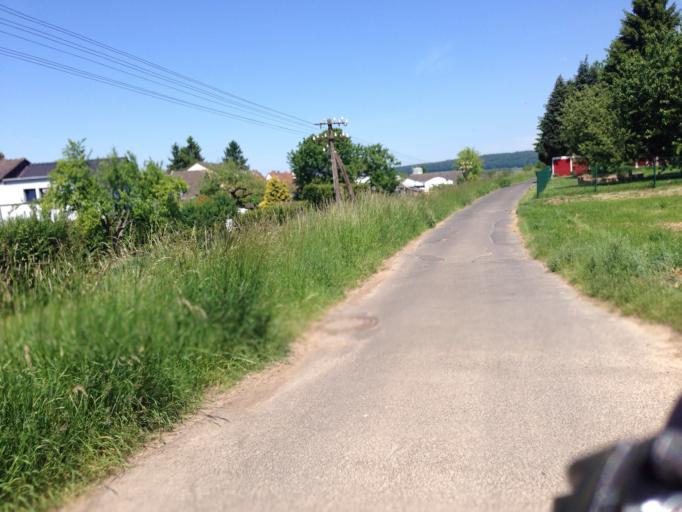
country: DE
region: Hesse
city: Budingen
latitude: 50.2823
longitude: 9.1122
